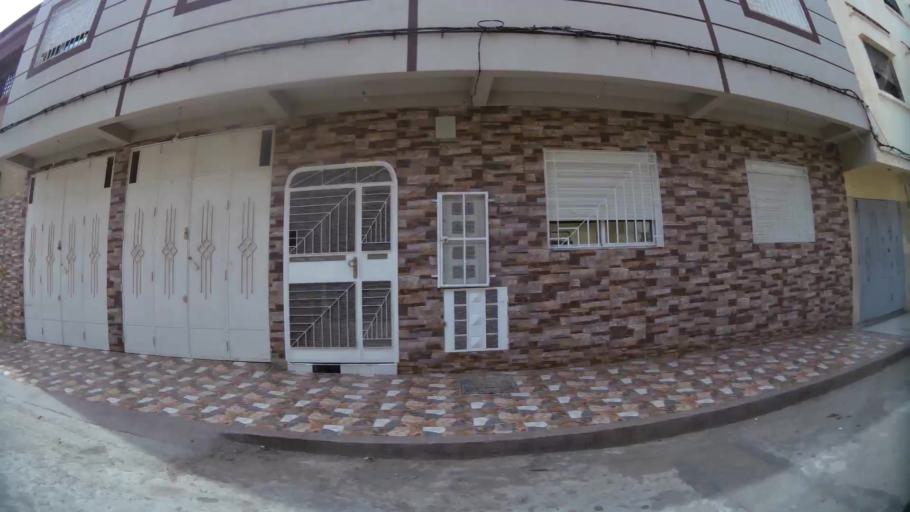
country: MA
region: Oriental
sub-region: Oujda-Angad
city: Oujda
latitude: 34.6865
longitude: -1.9044
